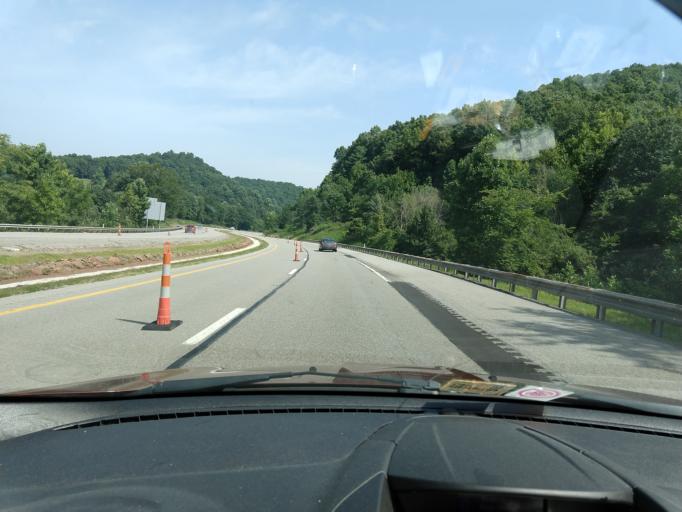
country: US
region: West Virginia
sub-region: Lewis County
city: Weston
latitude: 38.9925
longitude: -80.5051
